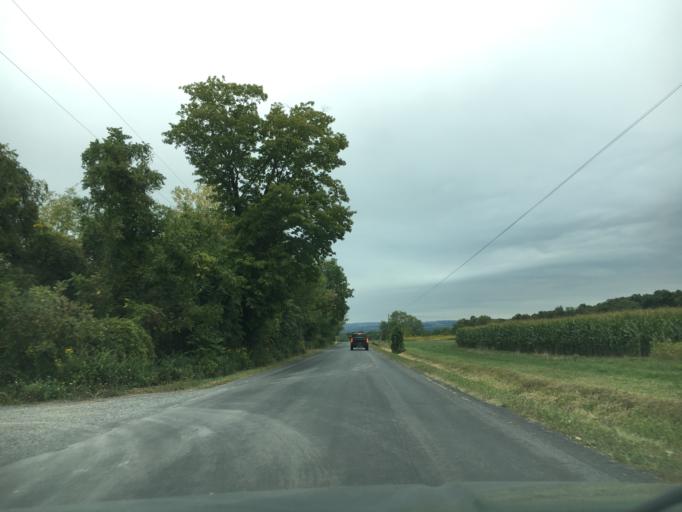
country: US
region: New York
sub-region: Tompkins County
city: Trumansburg
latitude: 42.6724
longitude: -76.7500
